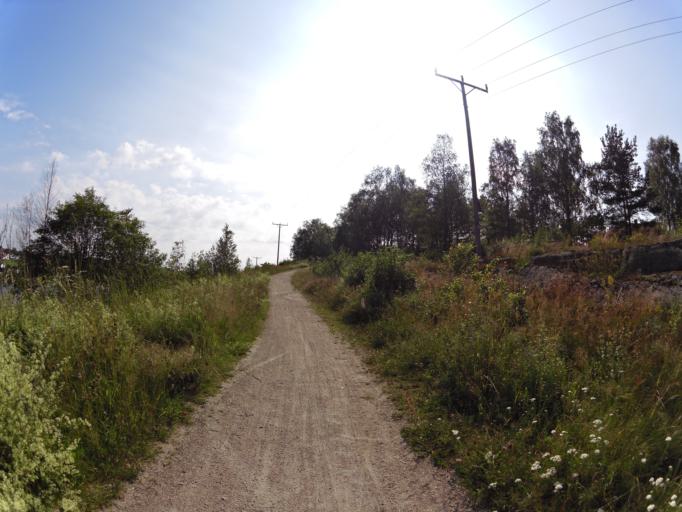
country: NO
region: Ostfold
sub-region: Fredrikstad
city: Fredrikstad
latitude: 59.2506
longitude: 11.0123
